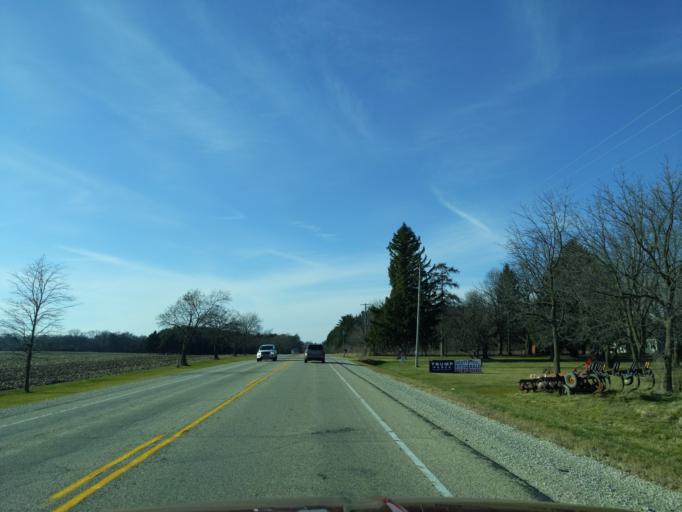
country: US
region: Wisconsin
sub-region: Walworth County
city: Whitewater
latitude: 42.8274
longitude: -88.7821
